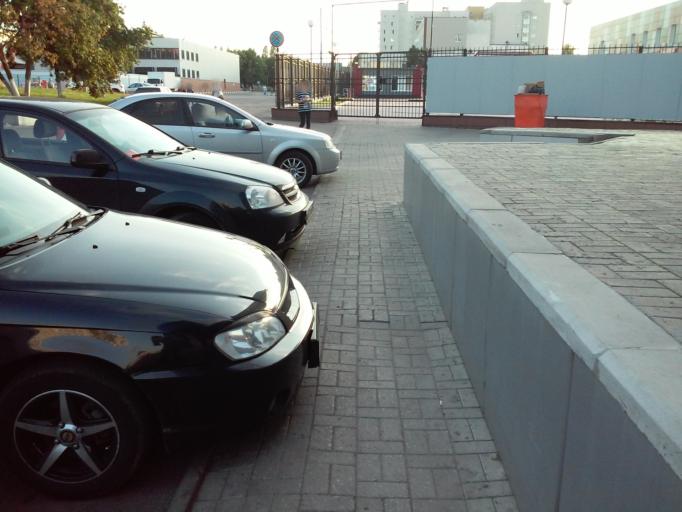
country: RU
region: Belgorod
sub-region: Belgorodskiy Rayon
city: Belgorod
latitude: 50.5750
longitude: 36.5822
